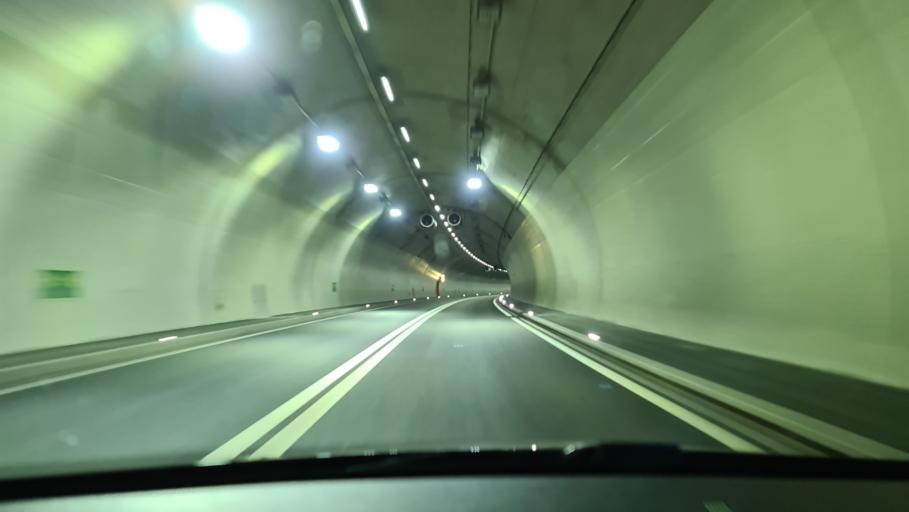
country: CH
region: Bern
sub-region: Jura bernois
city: Reconvilier
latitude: 47.2213
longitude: 7.2155
